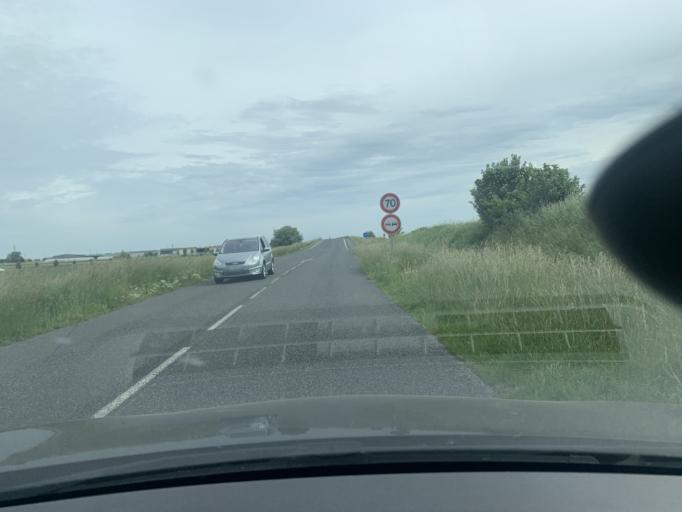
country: FR
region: Nord-Pas-de-Calais
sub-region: Departement du Nord
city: Rumilly-en-Cambresis
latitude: 50.1409
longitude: 3.2080
